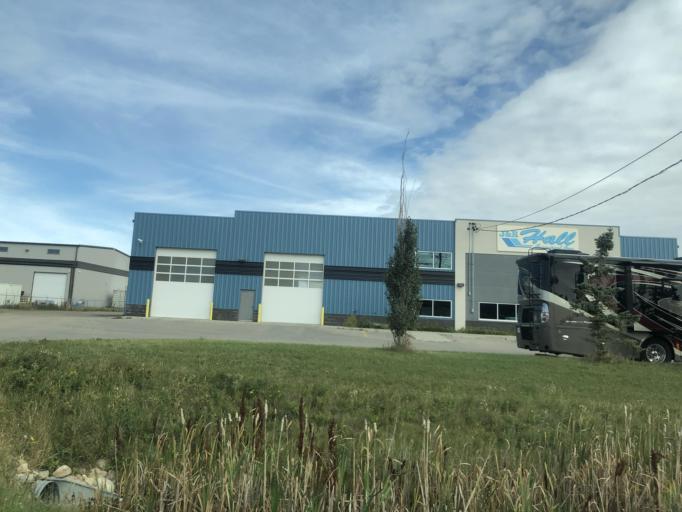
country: CA
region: Alberta
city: Chestermere
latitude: 50.9690
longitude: -113.9085
